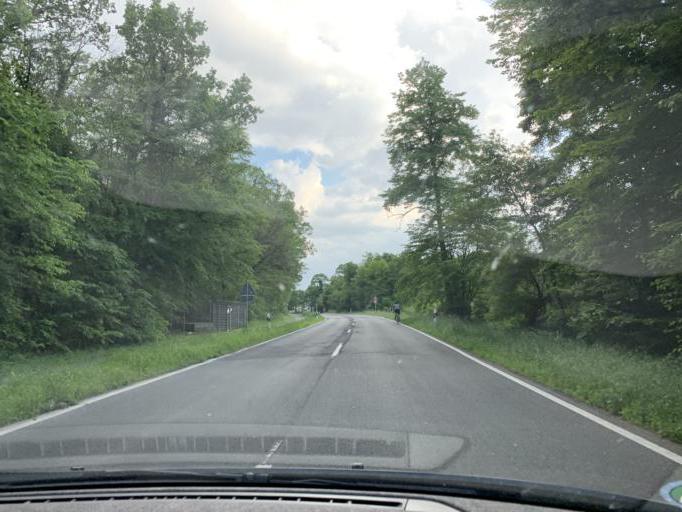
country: DE
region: North Rhine-Westphalia
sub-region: Regierungsbezirk Koln
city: Weilerswist
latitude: 50.7732
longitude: 6.8510
